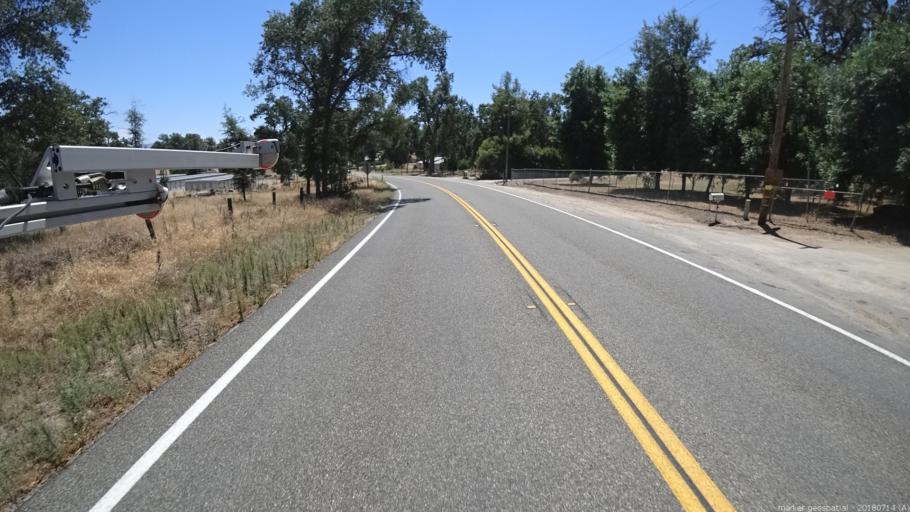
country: US
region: California
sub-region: Madera County
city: Ahwahnee
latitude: 37.3734
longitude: -119.7292
